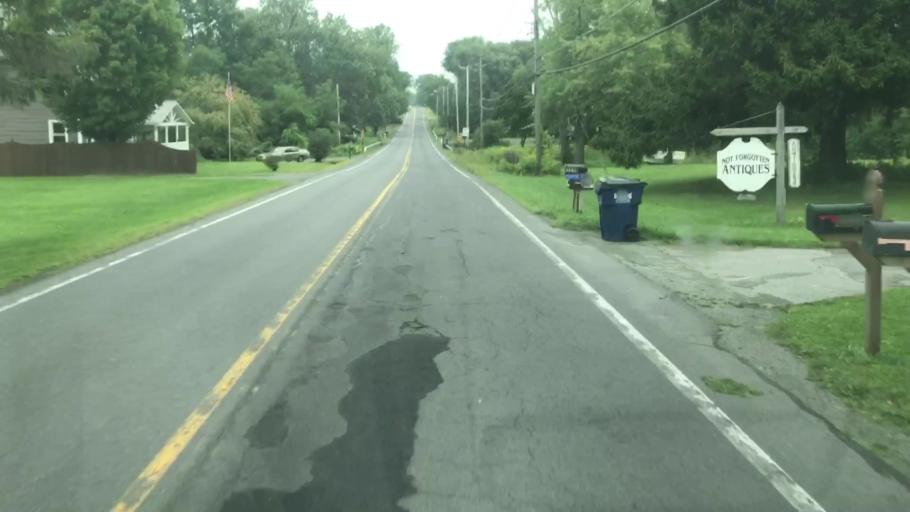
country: US
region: New York
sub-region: Cayuga County
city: Melrose Park
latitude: 42.9478
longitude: -76.5273
